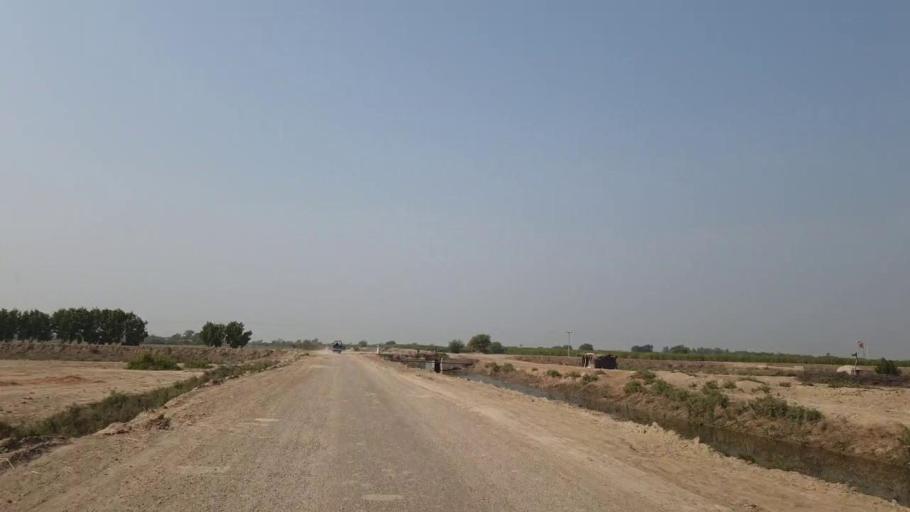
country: PK
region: Sindh
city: Tando Muhammad Khan
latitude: 24.9723
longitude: 68.5072
